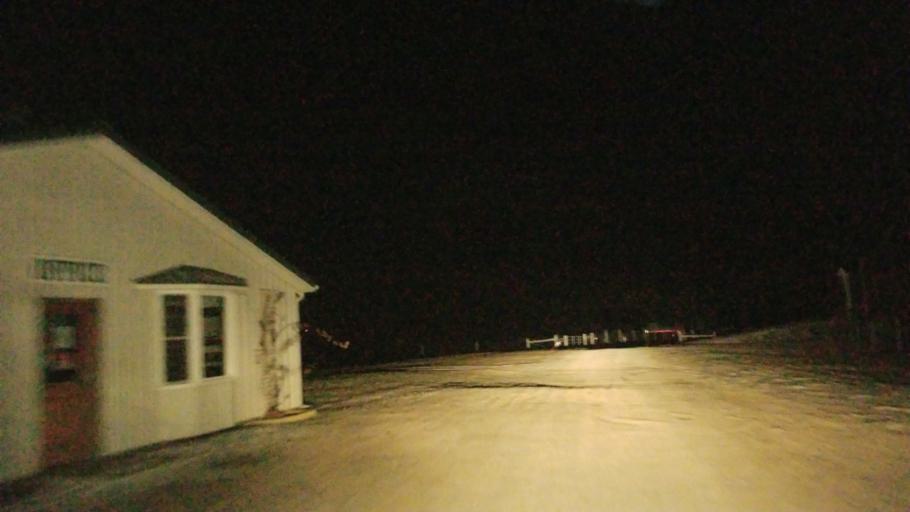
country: US
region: Michigan
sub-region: Osceola County
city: Evart
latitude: 43.8511
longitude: -85.3770
